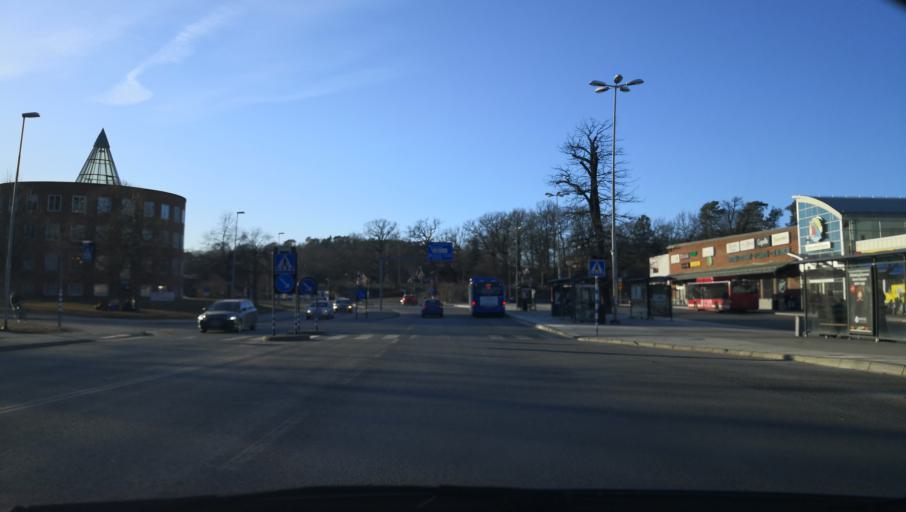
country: SE
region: Stockholm
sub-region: Varmdo Kommun
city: Gustavsberg
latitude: 59.3261
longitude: 18.3918
